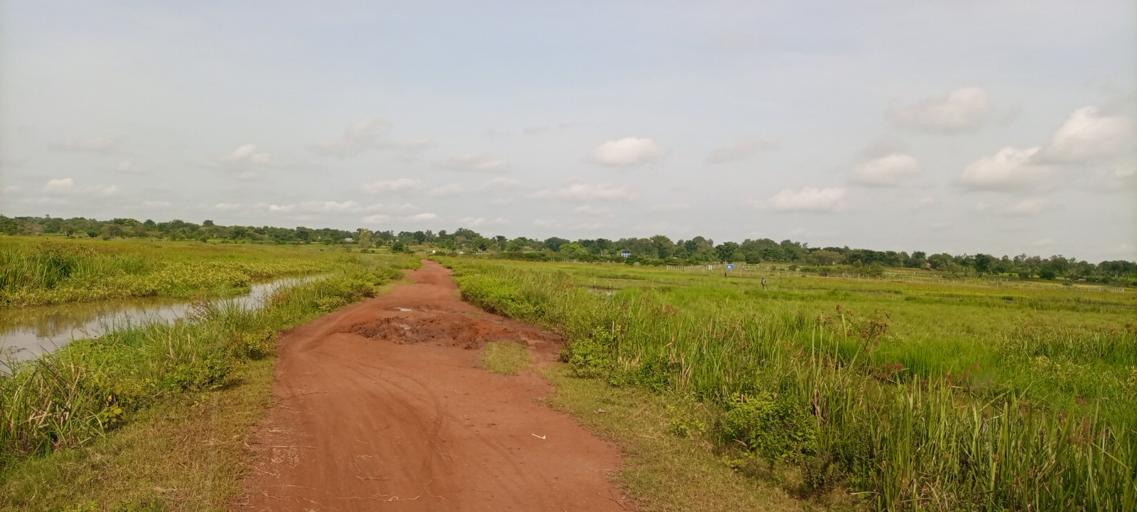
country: UG
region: Eastern Region
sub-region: Kibuku District
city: Kibuku
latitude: 1.0988
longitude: 33.7727
